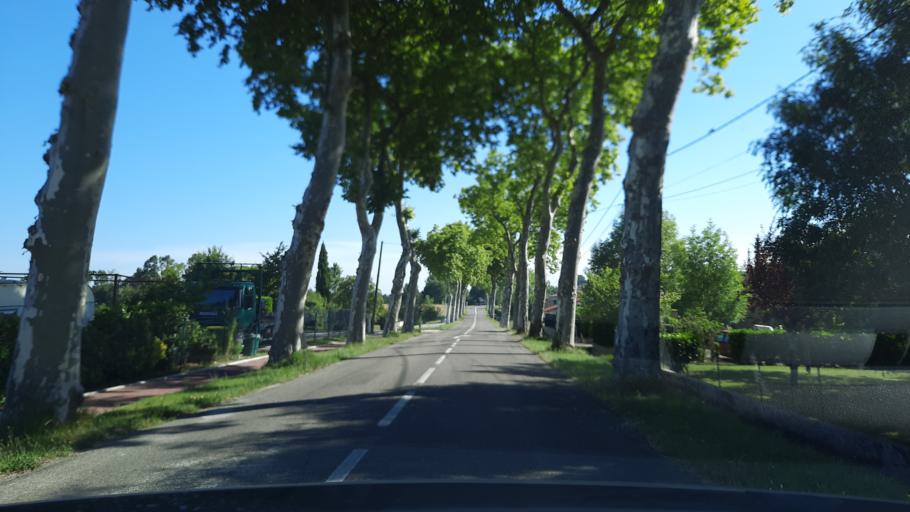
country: FR
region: Midi-Pyrenees
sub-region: Departement du Tarn-et-Garonne
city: Molieres
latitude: 44.1968
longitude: 1.3713
